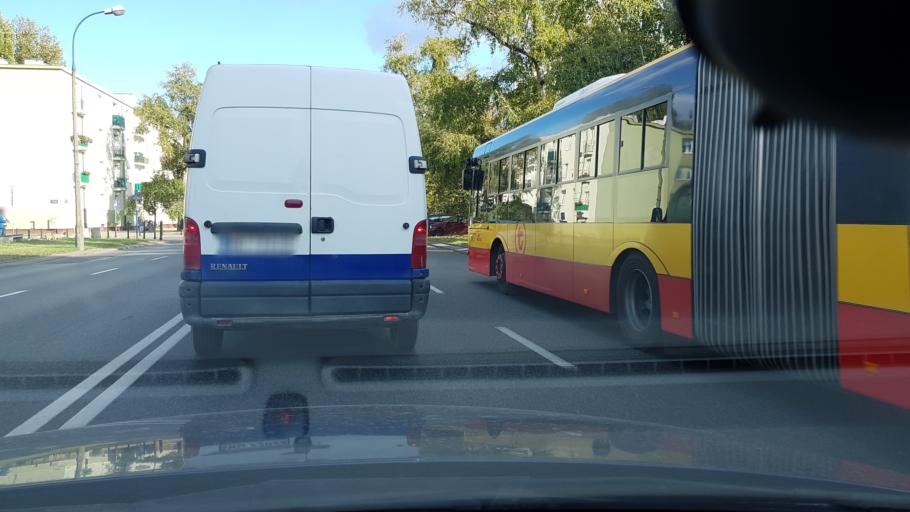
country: PL
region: Masovian Voivodeship
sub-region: Warszawa
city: Bielany
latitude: 52.2769
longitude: 20.9486
